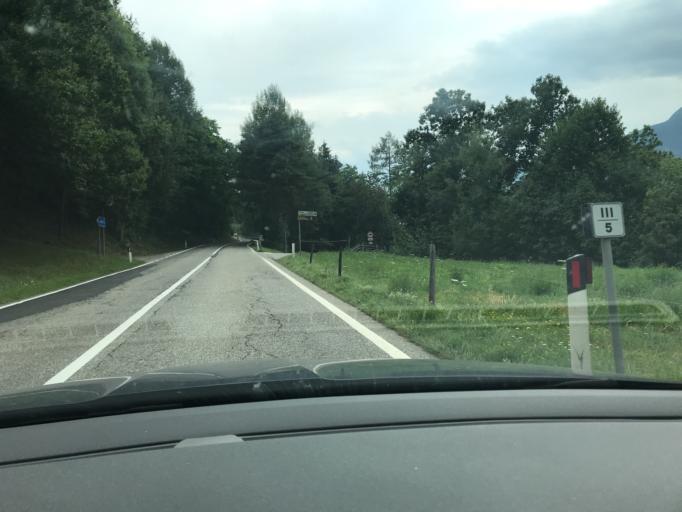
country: IT
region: Trentino-Alto Adige
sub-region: Bolzano
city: Villandro
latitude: 46.6151
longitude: 11.5460
